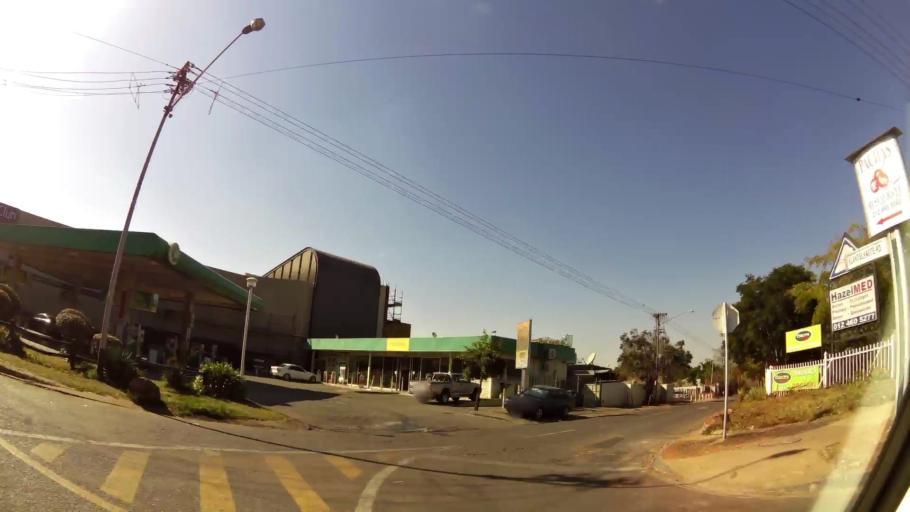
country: ZA
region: Gauteng
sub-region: City of Tshwane Metropolitan Municipality
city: Pretoria
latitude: -25.7790
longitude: 28.2568
